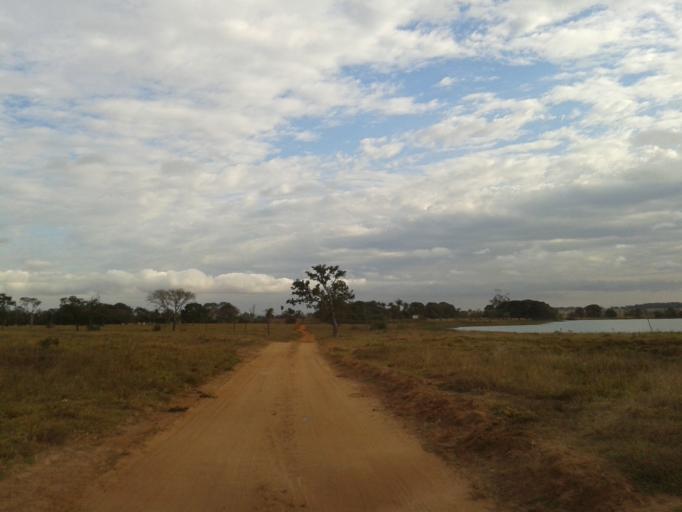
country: BR
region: Minas Gerais
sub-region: Santa Vitoria
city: Santa Vitoria
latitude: -18.7489
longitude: -50.2073
